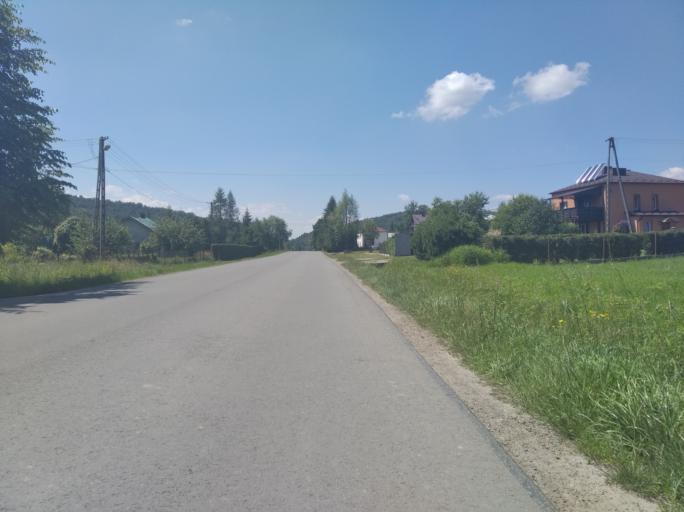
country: PL
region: Subcarpathian Voivodeship
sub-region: Powiat brzozowski
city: Niebocko
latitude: 49.6757
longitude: 22.0987
